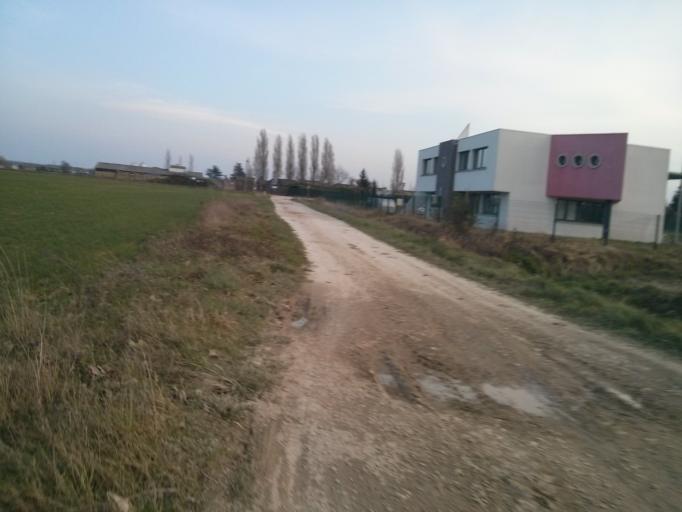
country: FR
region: Midi-Pyrenees
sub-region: Departement de la Haute-Garonne
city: Auzeville-Tolosane
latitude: 43.5328
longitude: 1.4969
